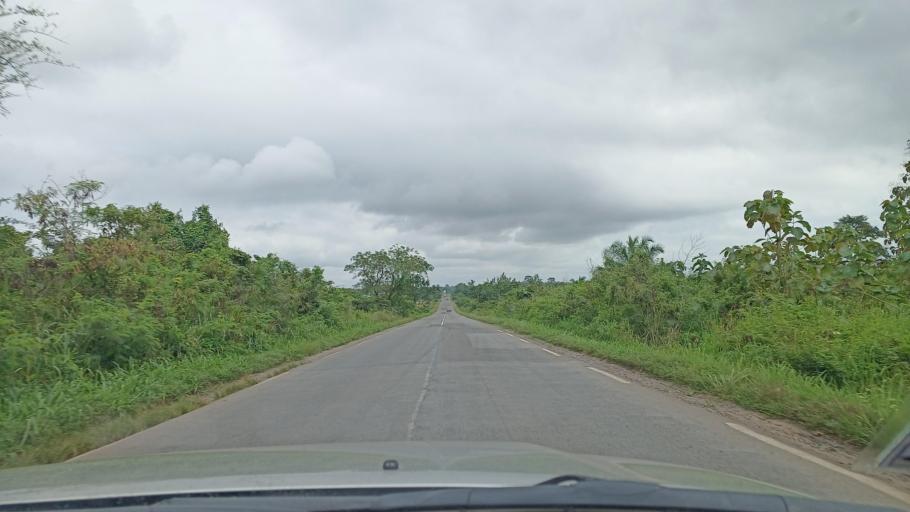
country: TG
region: Maritime
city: Tsevie
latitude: 6.5866
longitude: 1.1838
